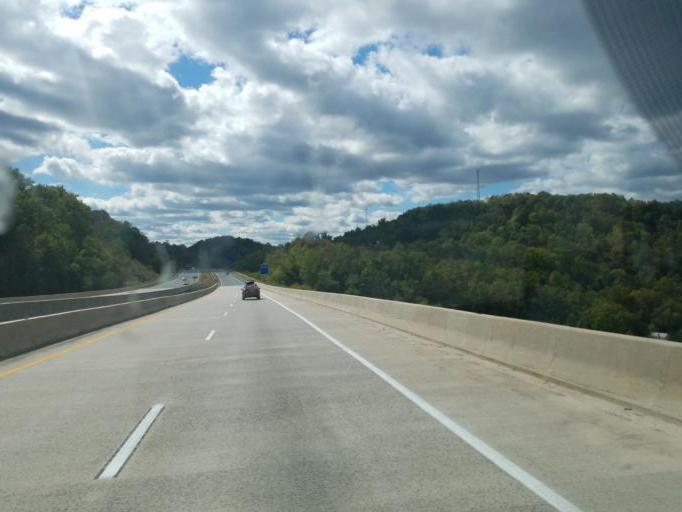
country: US
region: Maryland
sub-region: Allegany County
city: Cumberland
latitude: 39.6750
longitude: -78.6917
